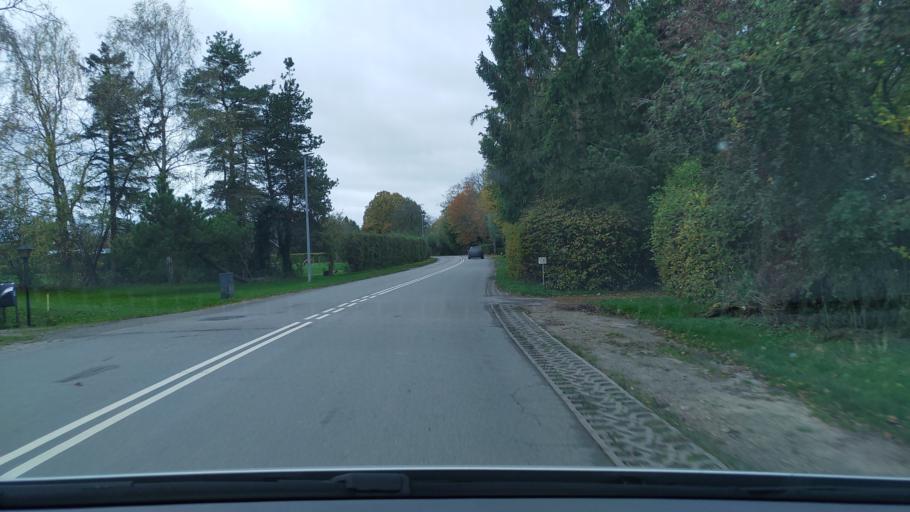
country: DK
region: Capital Region
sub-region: Tarnby Kommune
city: Tarnby
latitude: 55.6054
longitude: 12.6065
